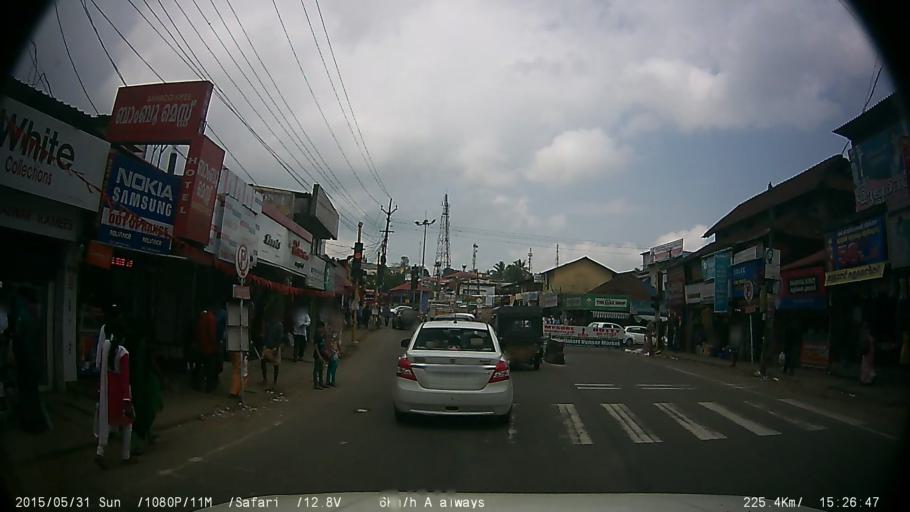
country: IN
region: Kerala
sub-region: Wayanad
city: Panamaram
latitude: 11.6630
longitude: 76.2566
